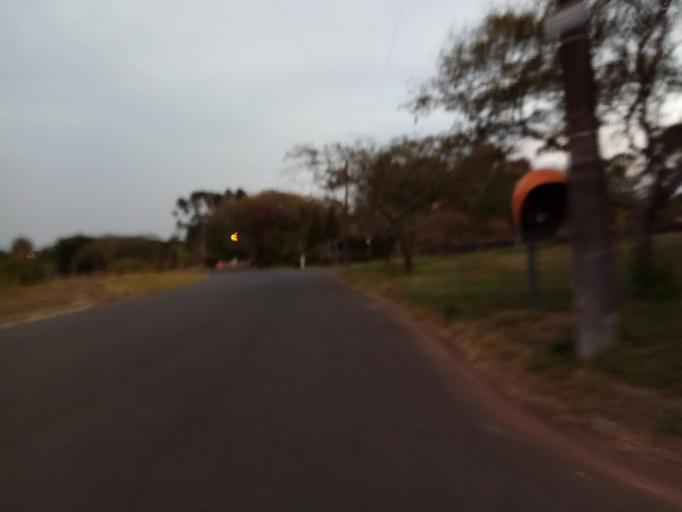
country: BR
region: Sao Paulo
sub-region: Piracicaba
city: Piracicaba
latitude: -22.7558
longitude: -47.5887
